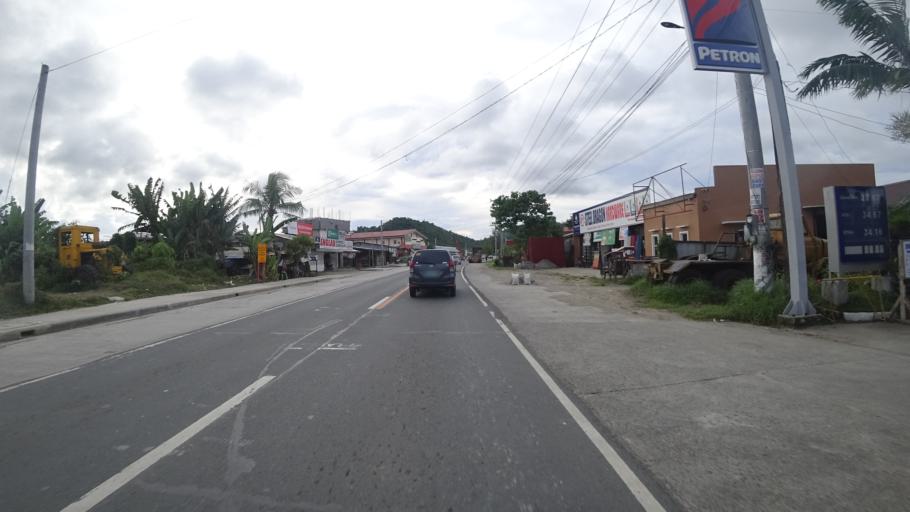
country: PH
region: Eastern Visayas
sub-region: Province of Leyte
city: Pawing
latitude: 11.1827
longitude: 124.9984
